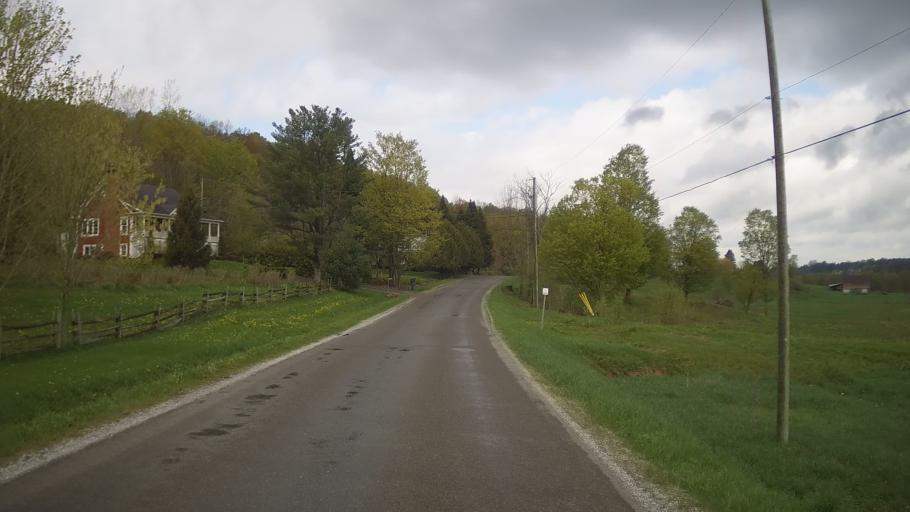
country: CA
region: Quebec
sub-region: Monteregie
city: Cowansville
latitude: 45.1912
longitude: -72.7007
